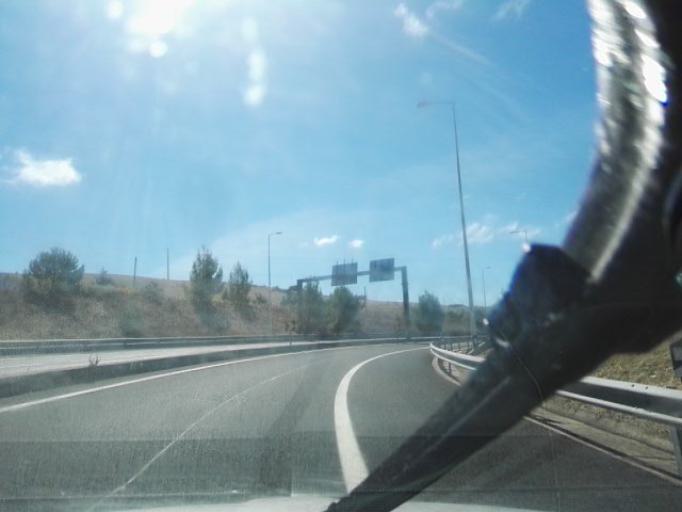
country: PT
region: Lisbon
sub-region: Arruda Dos Vinhos
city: Arruda dos Vinhos
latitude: 38.9667
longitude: -9.0604
